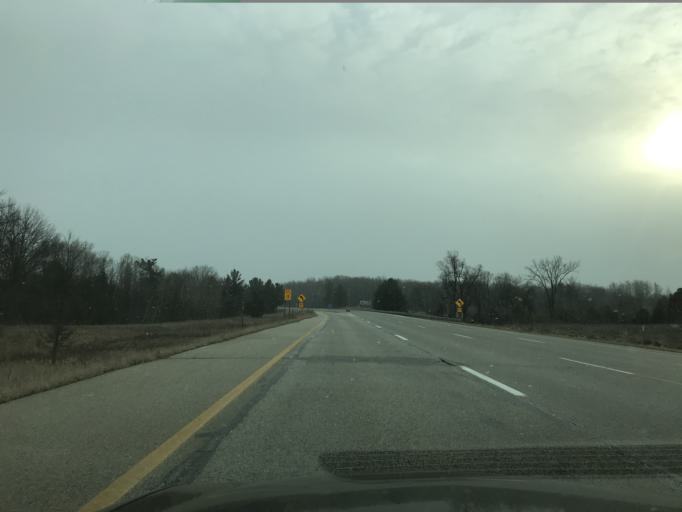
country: US
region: Michigan
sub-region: Clare County
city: Clare
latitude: 43.8553
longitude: -84.7789
